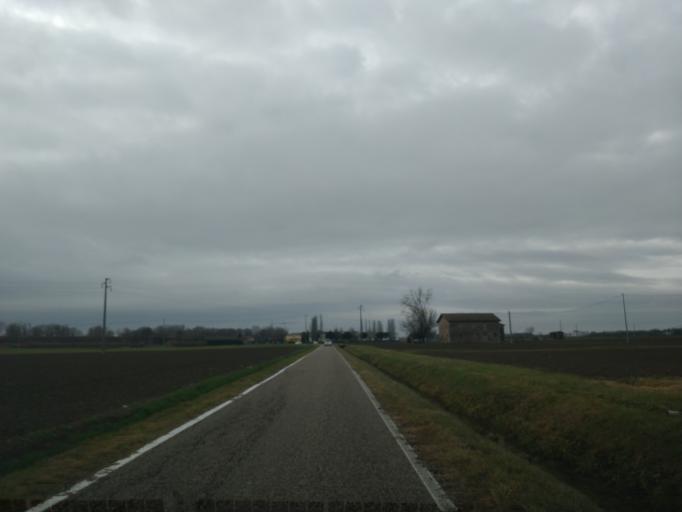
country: IT
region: Emilia-Romagna
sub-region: Provincia di Ferrara
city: Corpo Reno
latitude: 44.7511
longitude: 11.3203
